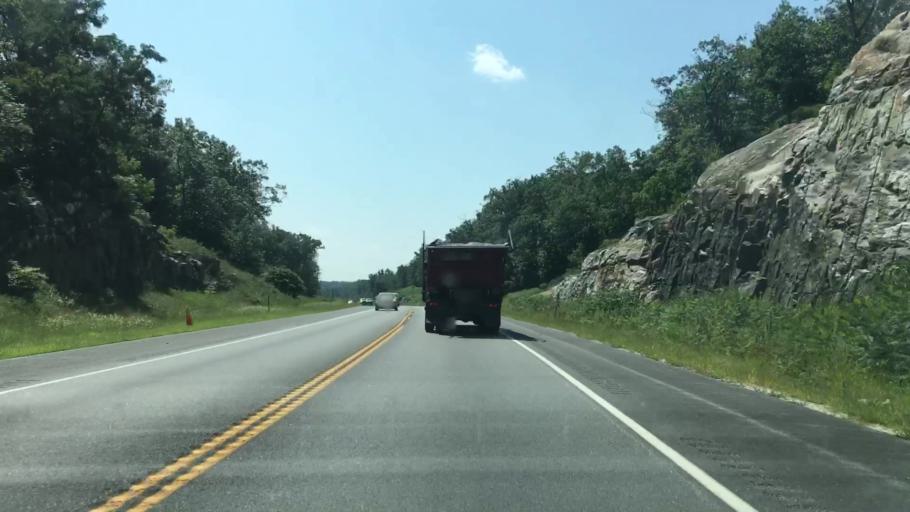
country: US
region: New Hampshire
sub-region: Rockingham County
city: Salem
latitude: 42.8291
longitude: -71.2397
